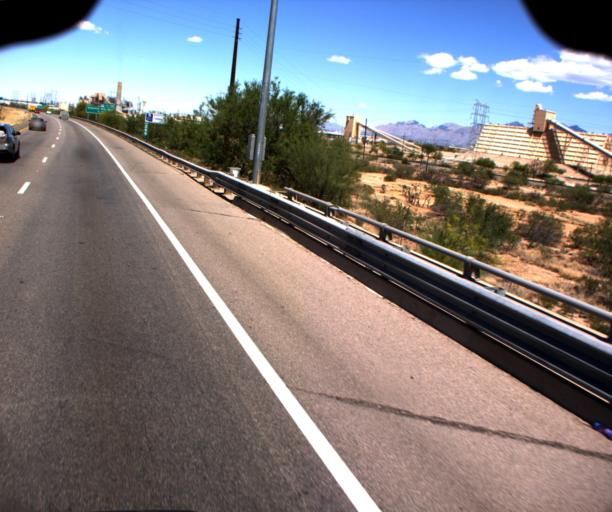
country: US
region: Arizona
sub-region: Pima County
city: Tucson
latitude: 32.1489
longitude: -110.8959
